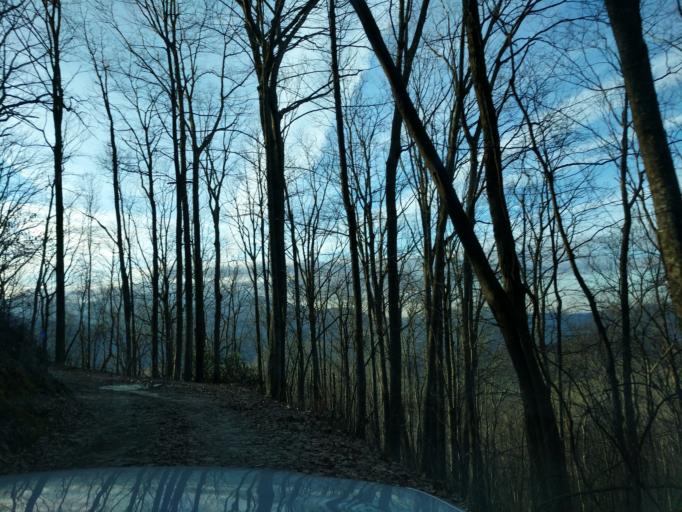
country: US
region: North Carolina
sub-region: Haywood County
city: Cove Creek
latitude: 35.7378
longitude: -83.0553
